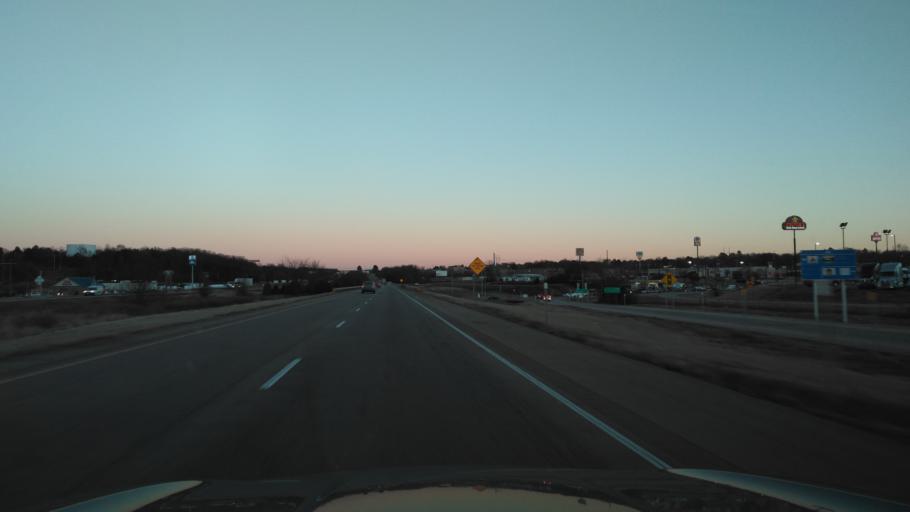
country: US
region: Arkansas
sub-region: Crawford County
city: Van Buren
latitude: 35.4629
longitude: -94.3593
